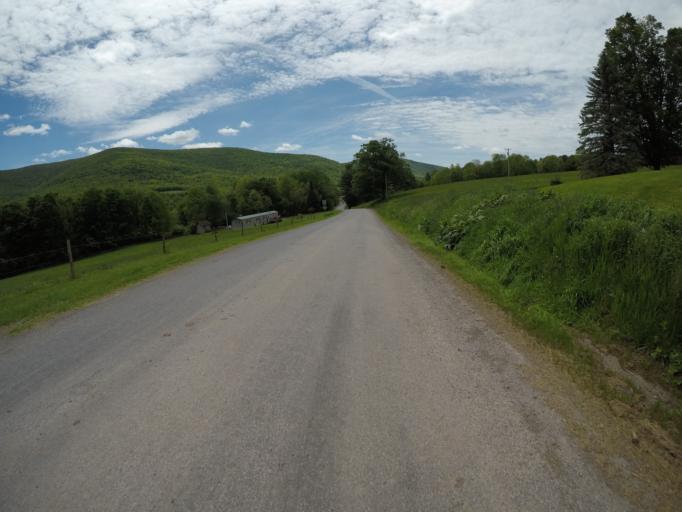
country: US
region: New York
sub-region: Delaware County
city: Stamford
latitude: 42.2642
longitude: -74.5201
